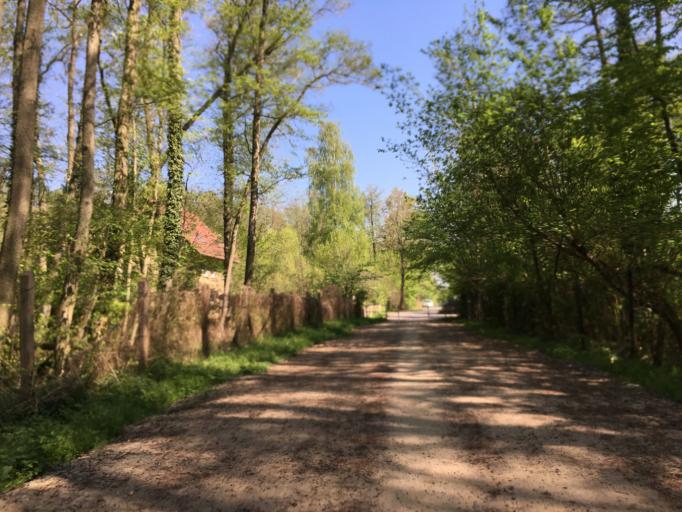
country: DE
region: Berlin
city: Buch
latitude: 52.6507
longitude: 13.5103
